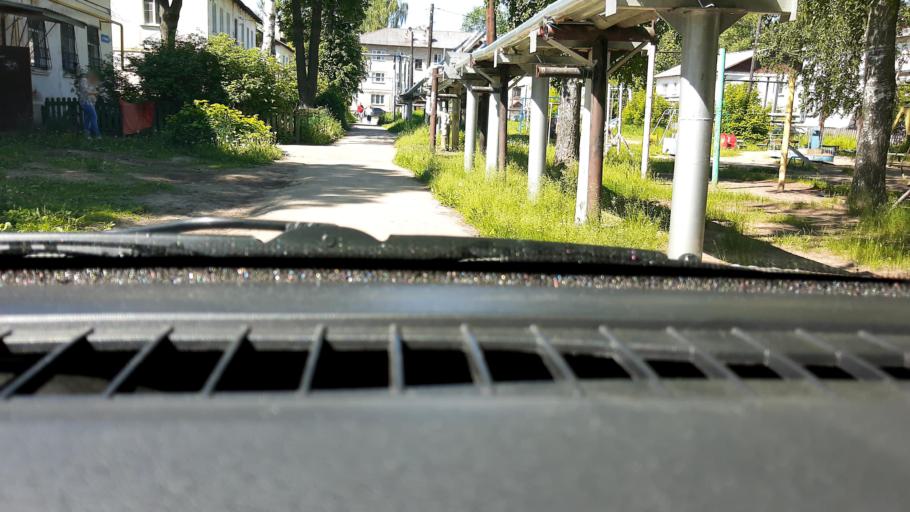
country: RU
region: Nizjnij Novgorod
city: Neklyudovo
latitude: 56.3481
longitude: 43.9069
